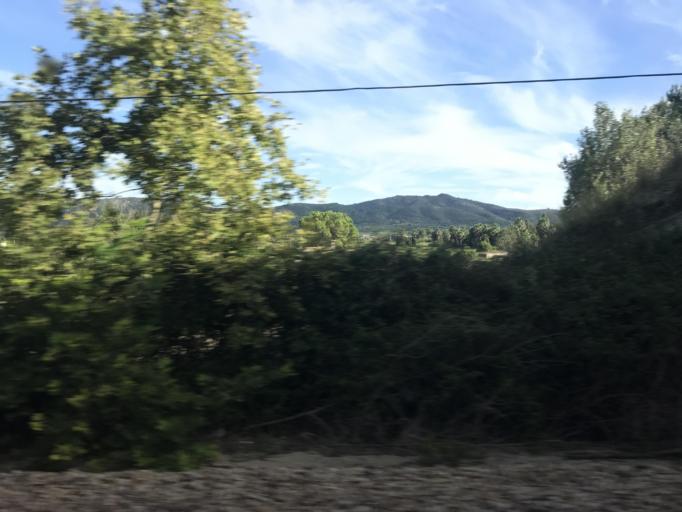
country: ES
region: Catalonia
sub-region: Provincia de Tarragona
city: Ulldecona
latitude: 40.6017
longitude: 0.4556
